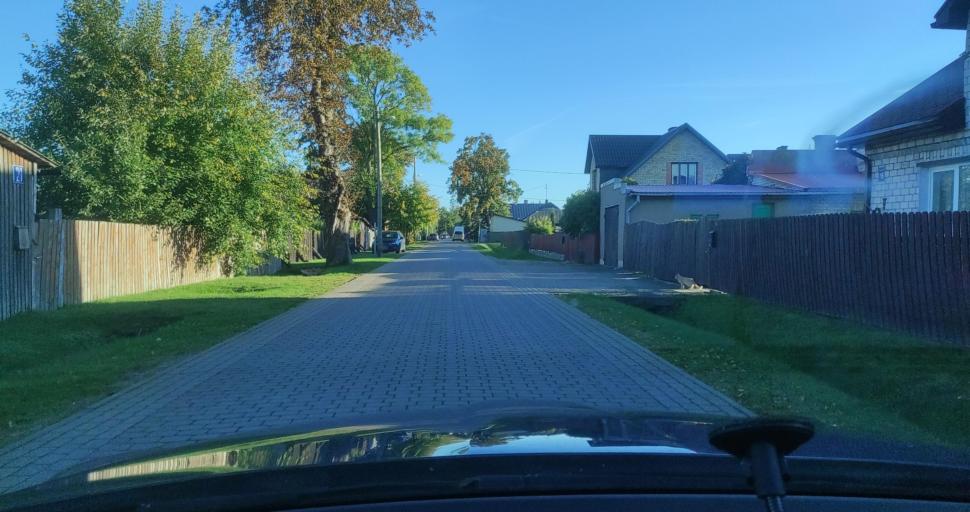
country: LV
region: Ventspils
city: Ventspils
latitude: 57.3788
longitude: 21.5748
